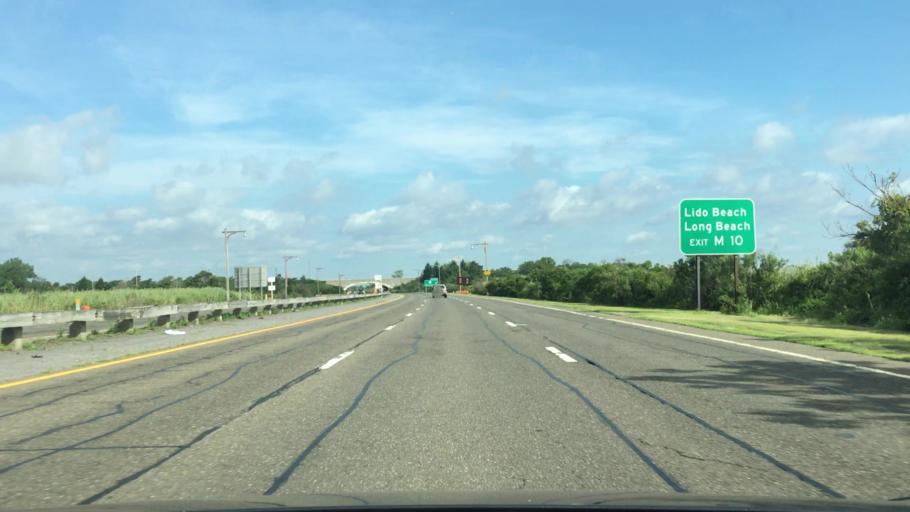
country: US
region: New York
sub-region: Nassau County
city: Point Lookout
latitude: 40.6070
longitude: -73.5461
